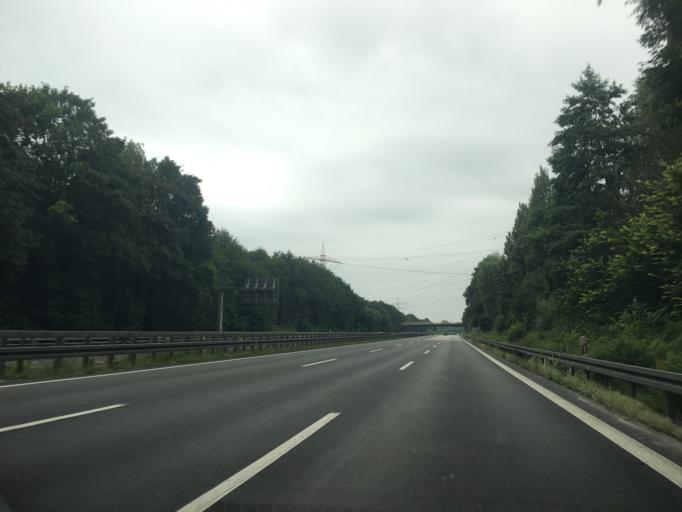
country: DE
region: North Rhine-Westphalia
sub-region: Regierungsbezirk Munster
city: Bottrop
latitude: 51.5032
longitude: 6.9317
